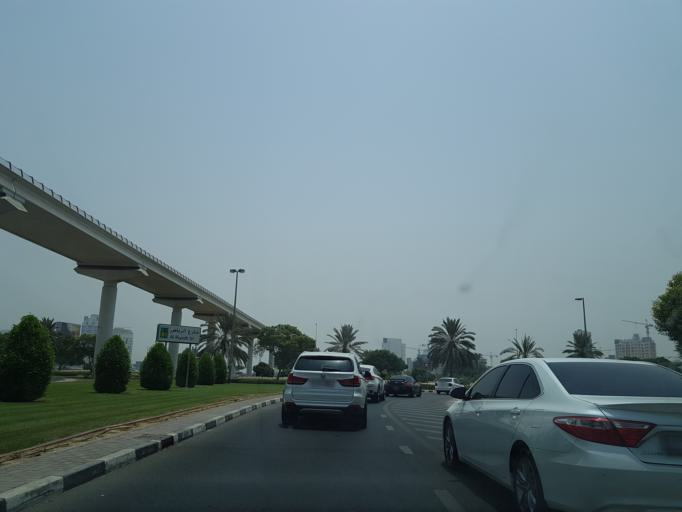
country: AE
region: Ash Shariqah
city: Sharjah
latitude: 25.2291
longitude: 55.3298
